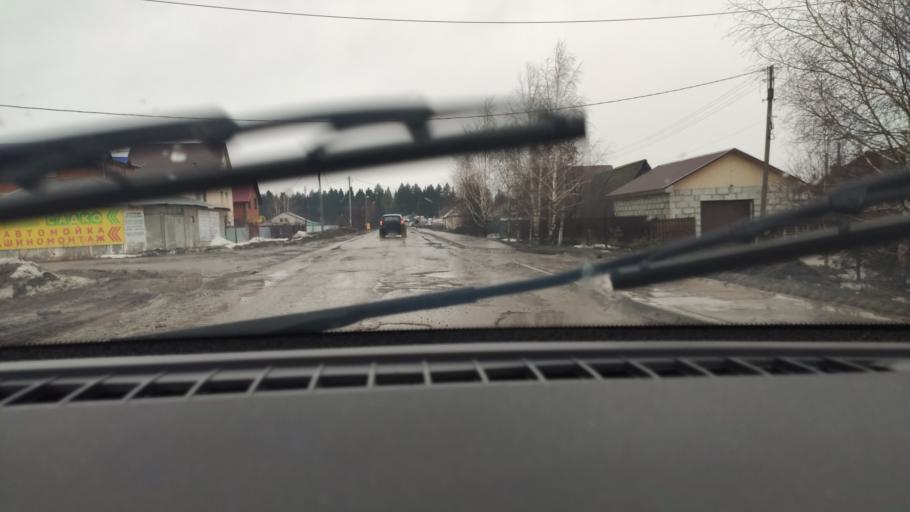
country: RU
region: Perm
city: Kultayevo
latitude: 57.8988
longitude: 55.9617
